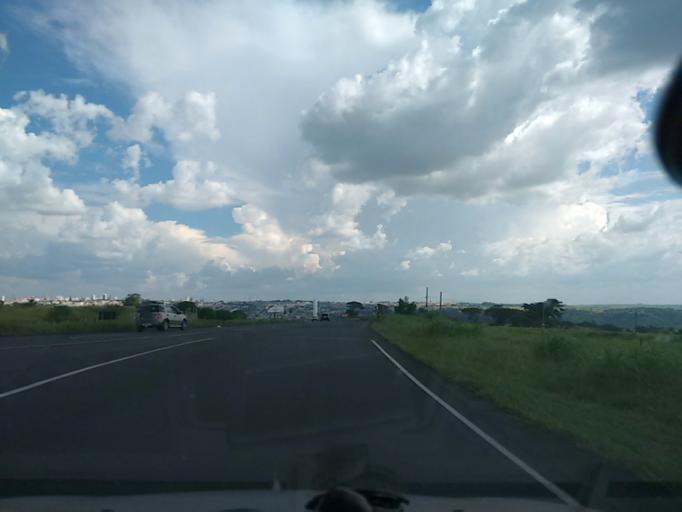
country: BR
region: Sao Paulo
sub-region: Marilia
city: Marilia
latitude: -22.1804
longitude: -49.9725
